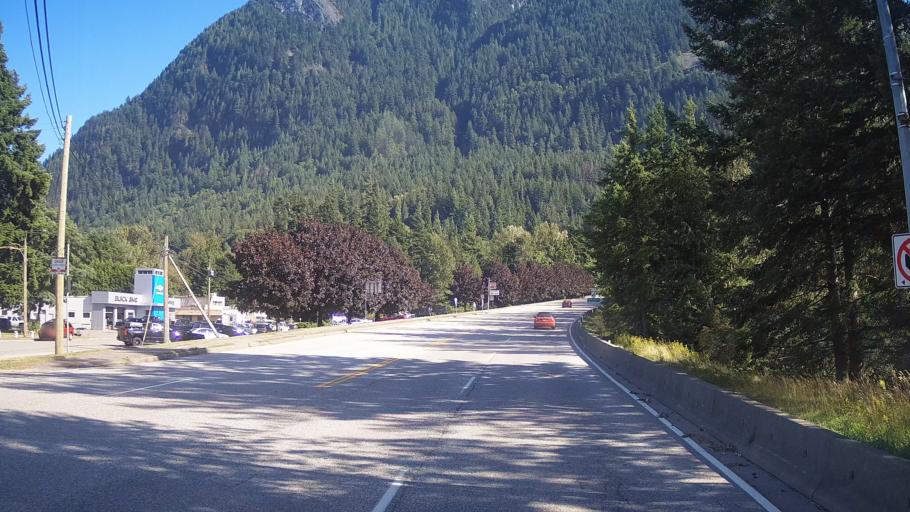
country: CA
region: British Columbia
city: Hope
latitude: 49.3770
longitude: -121.4433
